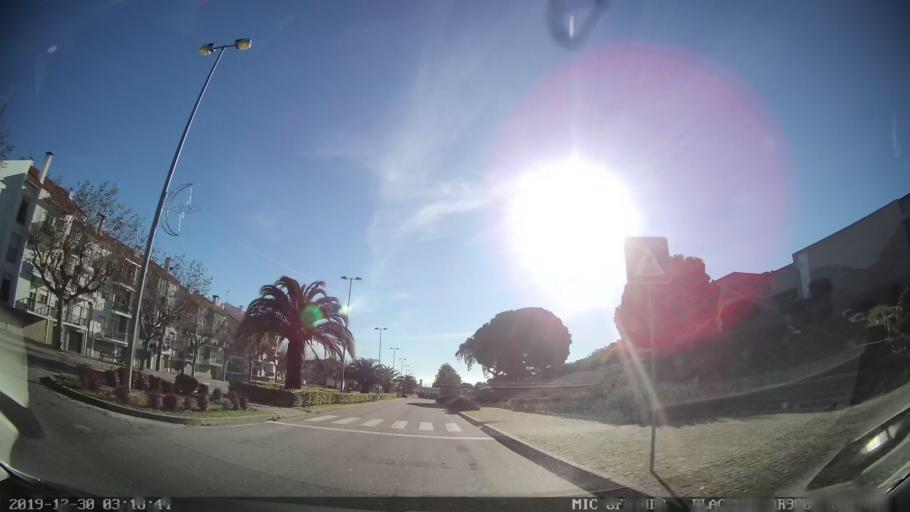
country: PT
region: Castelo Branco
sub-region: Idanha-A-Nova
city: Idanha-a-Nova
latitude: 39.9270
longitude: -7.2436
